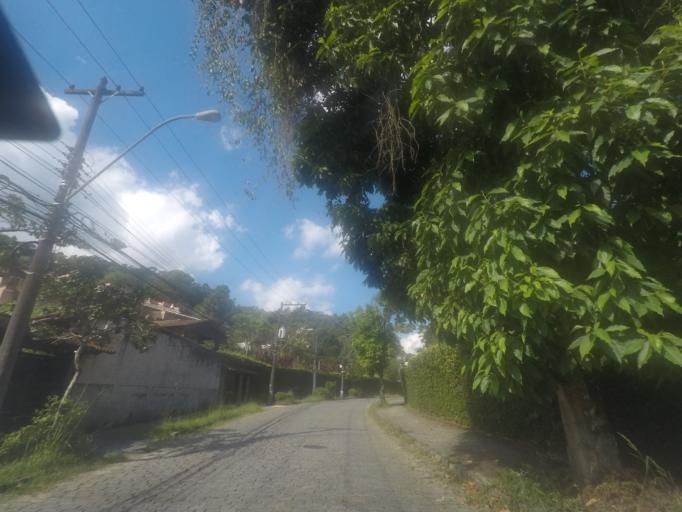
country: BR
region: Rio de Janeiro
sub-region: Petropolis
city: Petropolis
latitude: -22.5244
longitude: -43.2103
